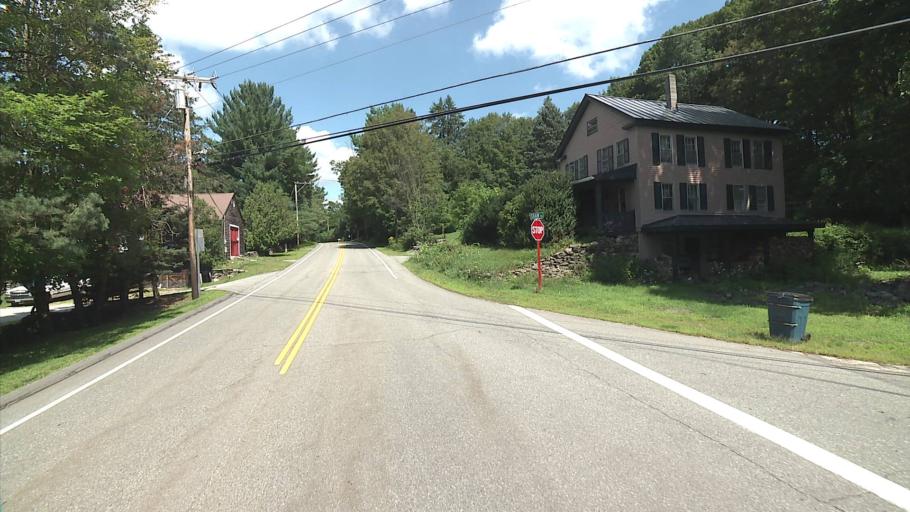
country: US
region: Connecticut
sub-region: Windham County
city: South Woodstock
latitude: 41.9422
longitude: -72.0741
